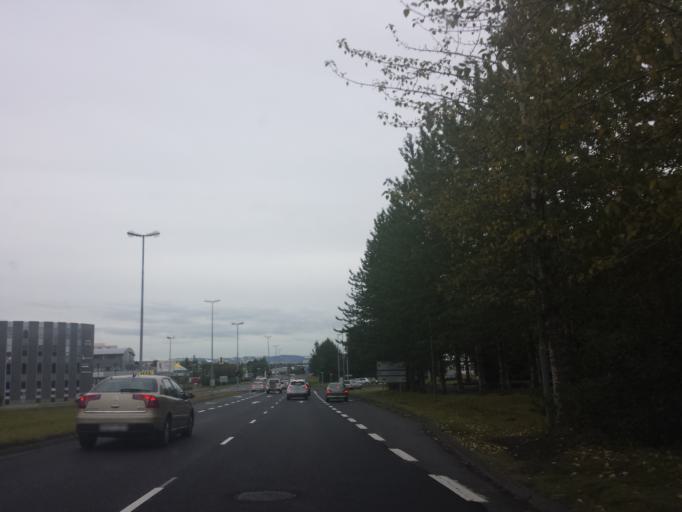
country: IS
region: Capital Region
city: Reykjavik
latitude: 64.1350
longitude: -21.8722
